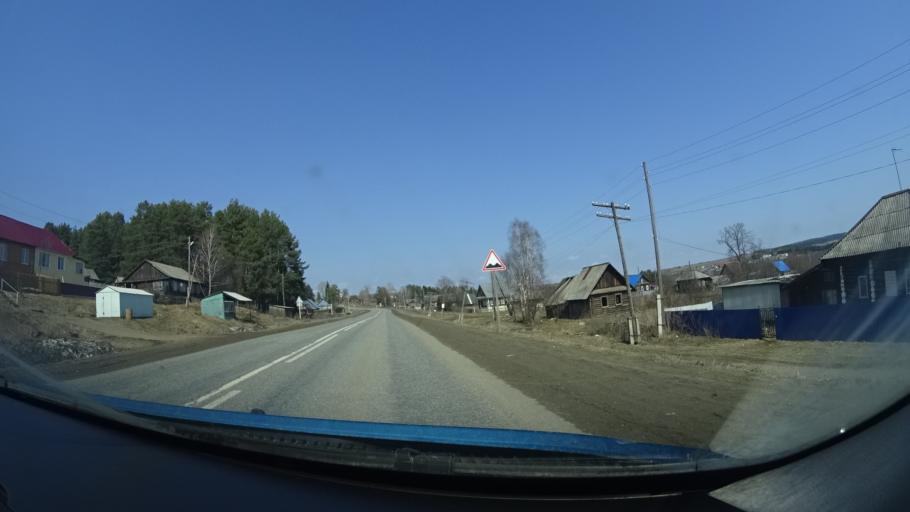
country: RU
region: Perm
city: Yugo-Kamskiy
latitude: 57.5509
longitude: 55.6853
